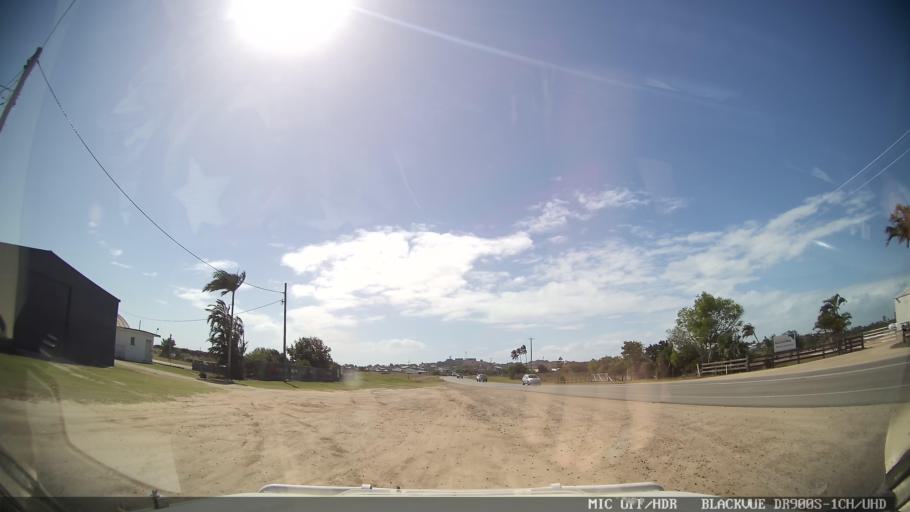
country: AU
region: Queensland
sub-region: Whitsunday
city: Bowen
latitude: -20.0127
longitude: 148.2247
